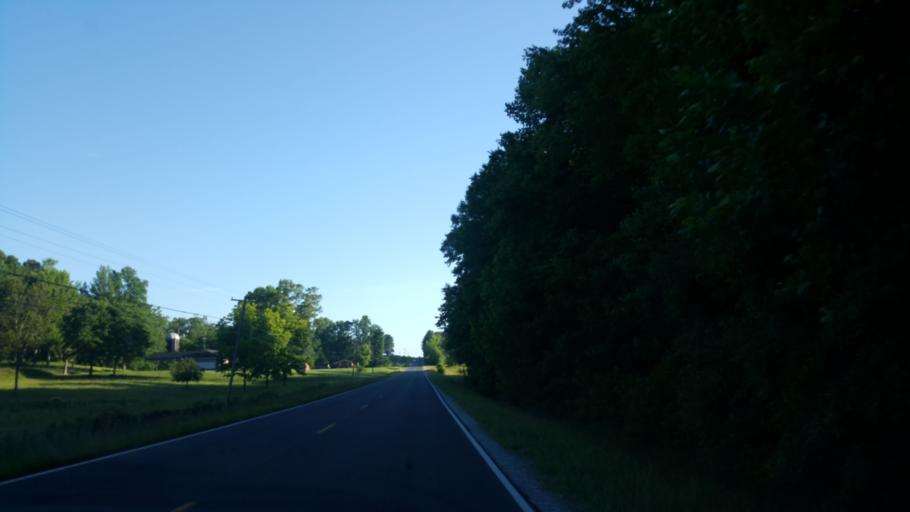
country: US
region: Tennessee
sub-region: Henderson County
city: Lexington
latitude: 35.5554
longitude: -88.3855
